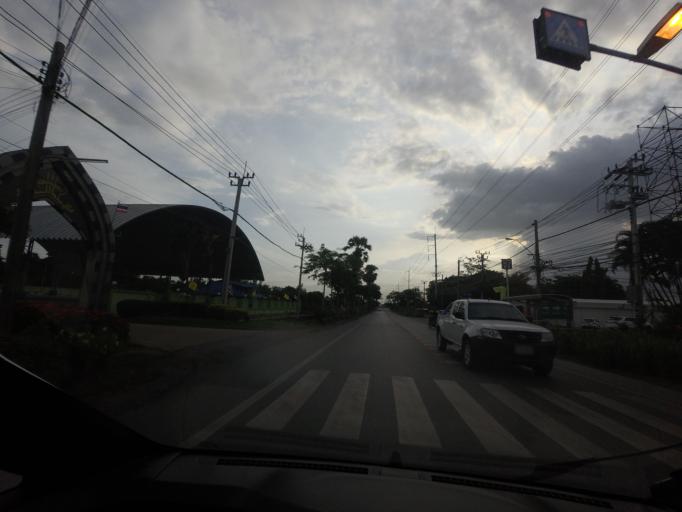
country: TH
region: Bangkok
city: Nong Chok
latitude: 13.8574
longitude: 100.8332
